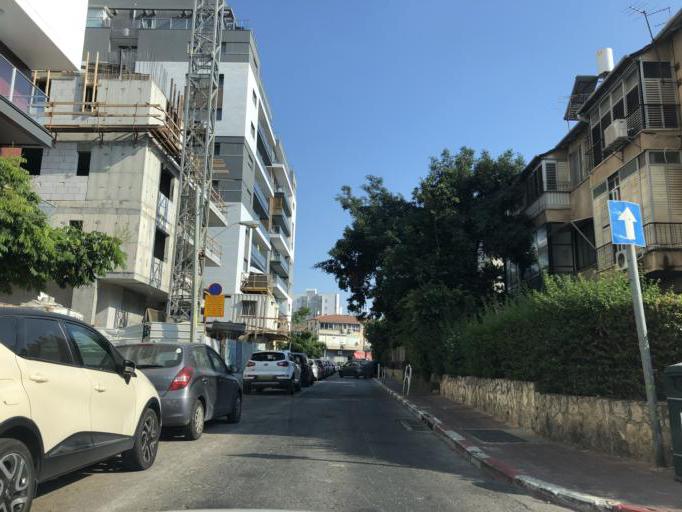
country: IL
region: Tel Aviv
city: Bene Beraq
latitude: 32.0841
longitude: 34.8249
